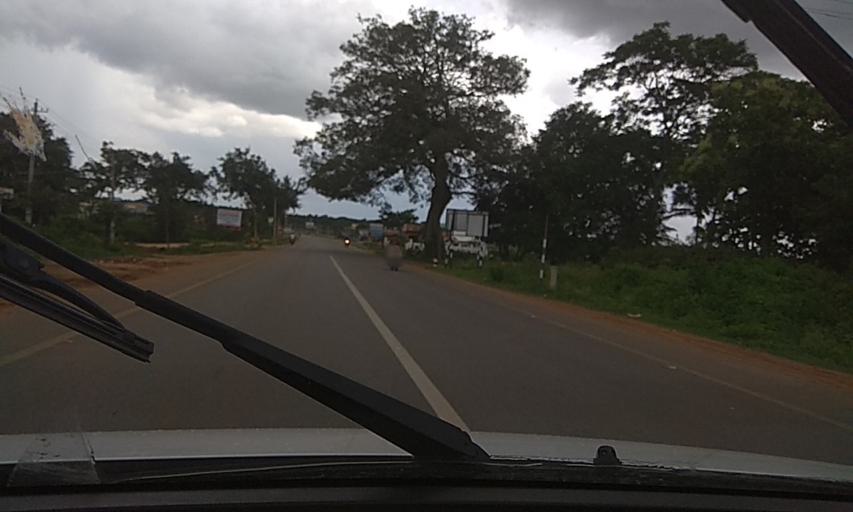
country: IN
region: Karnataka
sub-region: Tumkur
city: Kunigal
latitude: 13.1647
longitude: 77.0318
